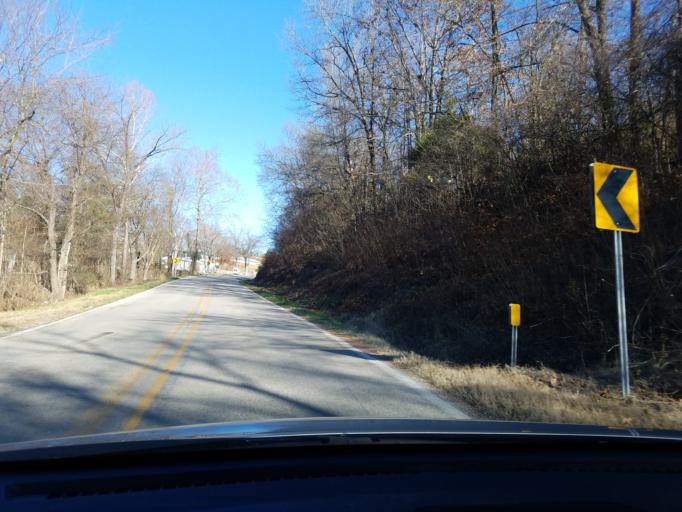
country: US
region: Missouri
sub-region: Stone County
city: Kimberling City
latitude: 36.4873
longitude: -93.4056
